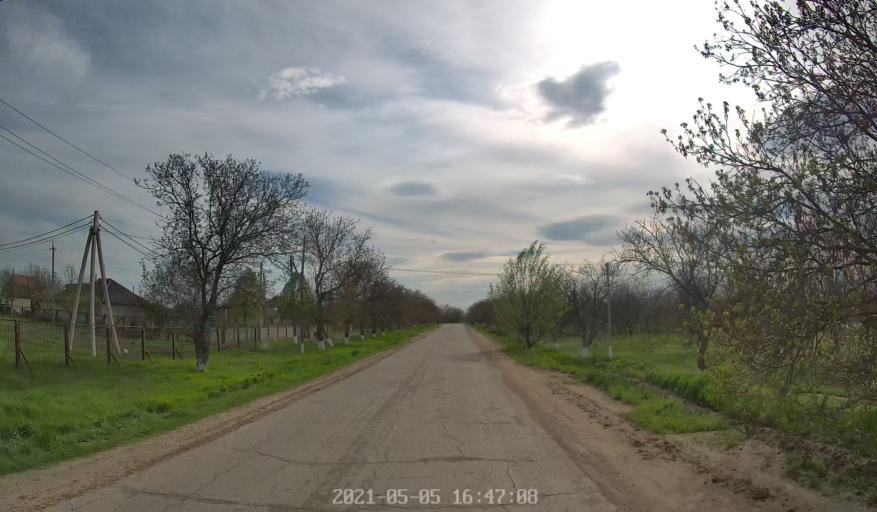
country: MD
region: Chisinau
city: Vadul lui Voda
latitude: 47.0955
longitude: 29.1831
